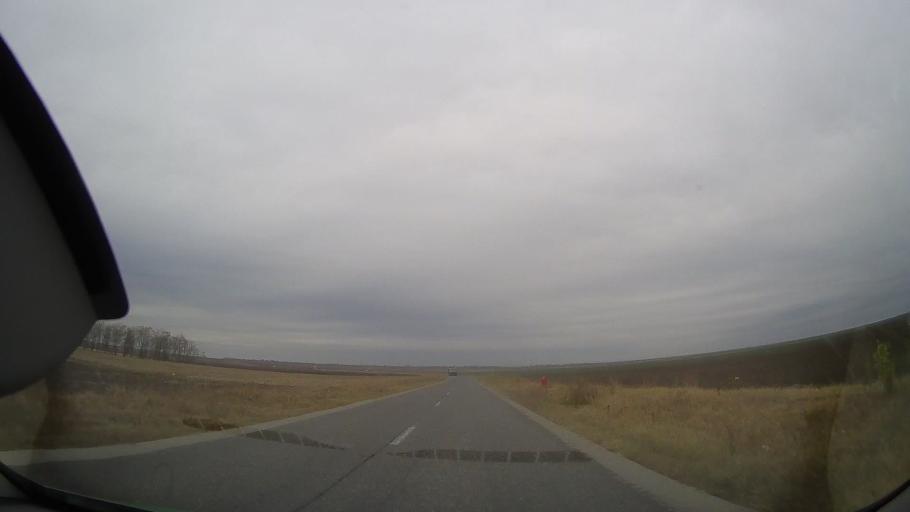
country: RO
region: Ialomita
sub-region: Comuna Milosesti
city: Milosesti
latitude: 44.7432
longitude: 27.2529
